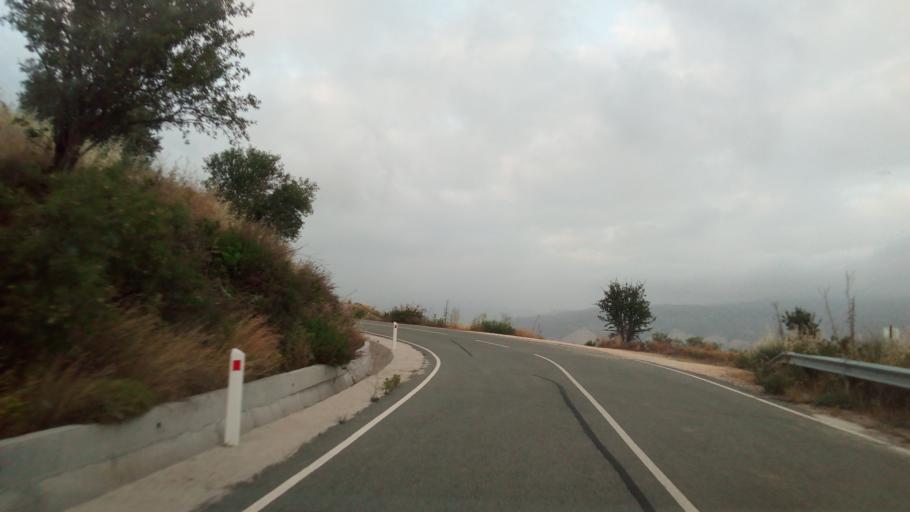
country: CY
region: Limassol
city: Pachna
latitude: 34.8624
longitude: 32.6451
